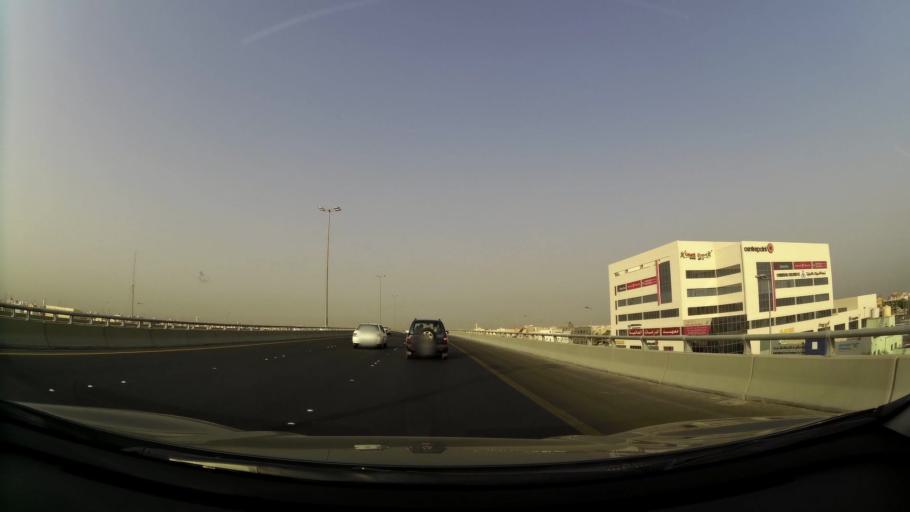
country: KW
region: Al Asimah
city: Ar Rabiyah
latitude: 29.3108
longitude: 47.8641
